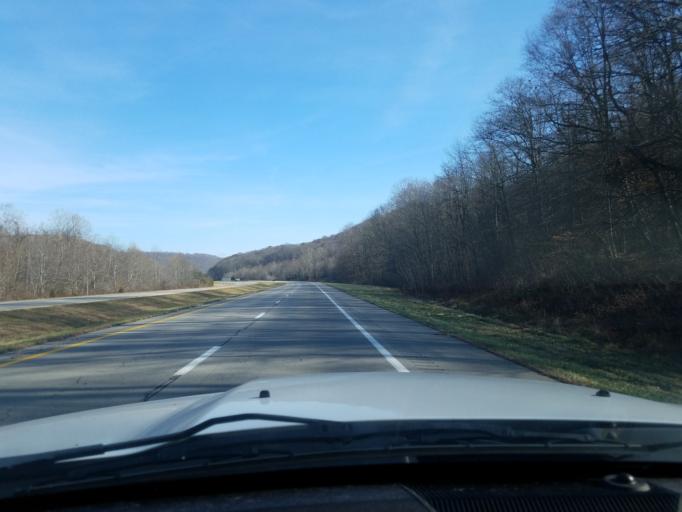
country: US
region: Ohio
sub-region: Adams County
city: Peebles
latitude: 39.0438
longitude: -83.2226
